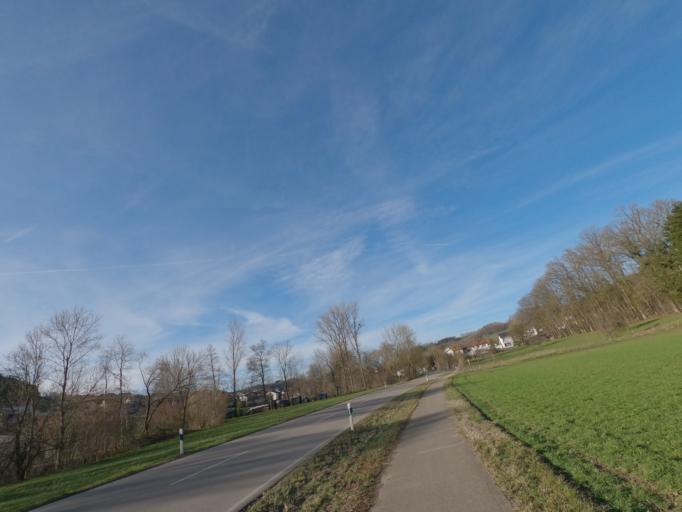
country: DE
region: Baden-Wuerttemberg
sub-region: Regierungsbezirk Stuttgart
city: Donzdorf
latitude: 48.7035
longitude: 9.7984
